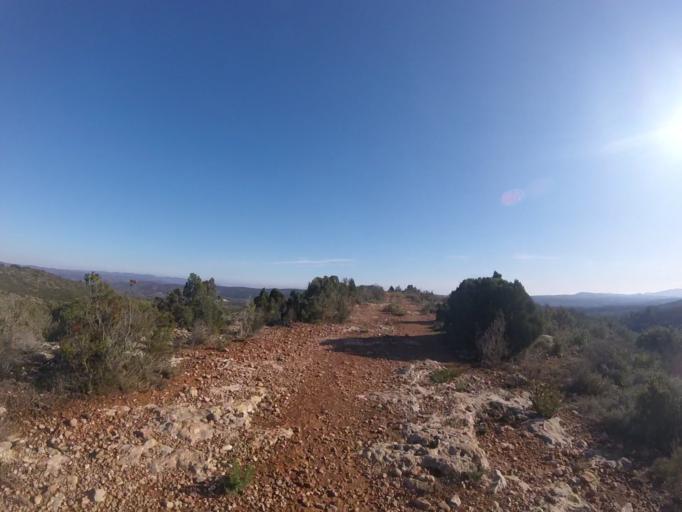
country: ES
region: Valencia
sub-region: Provincia de Castello
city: Sarratella
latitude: 40.2899
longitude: 0.0544
